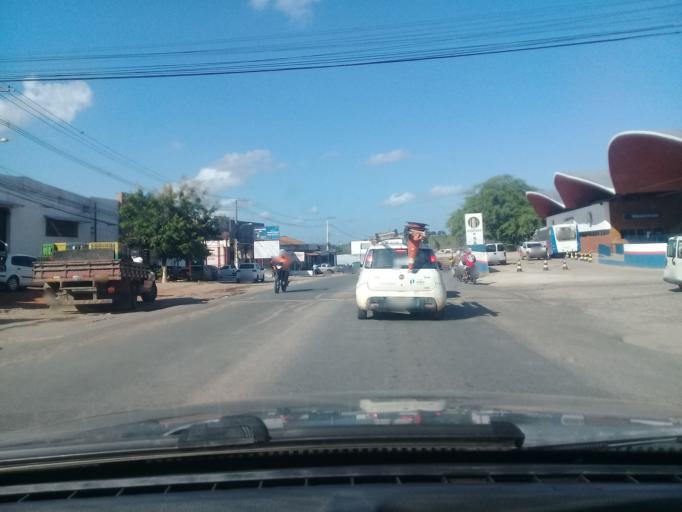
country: BR
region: Pernambuco
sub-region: Vitoria De Santo Antao
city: Vitoria de Santo Antao
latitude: -8.1126
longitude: -35.2926
